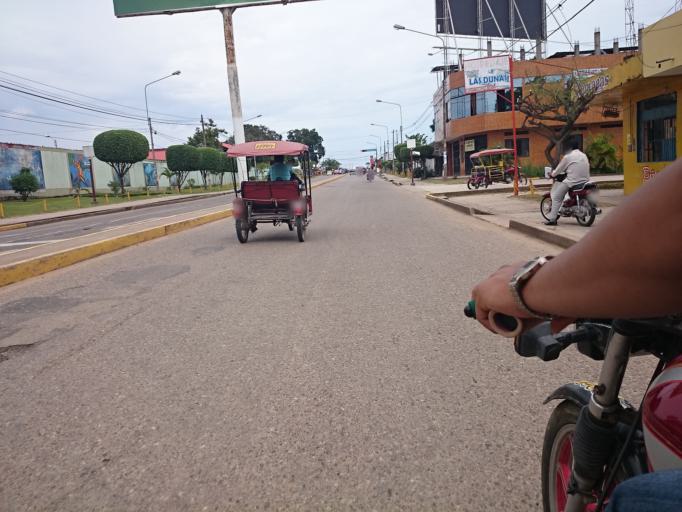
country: PE
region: Ucayali
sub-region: Provincia de Coronel Portillo
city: Puerto Callao
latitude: -8.3605
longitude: -74.5706
